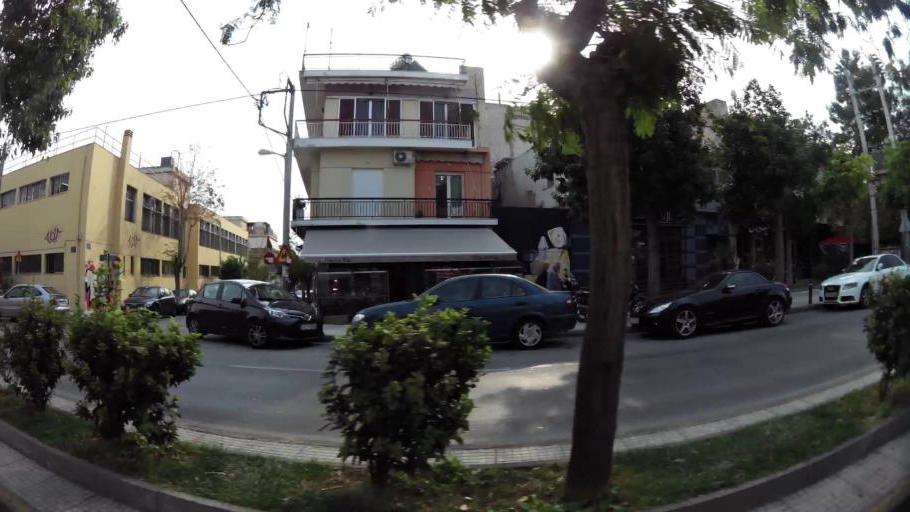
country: GR
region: Attica
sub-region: Nomarchia Athinas
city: Aigaleo
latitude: 37.9937
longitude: 23.6792
